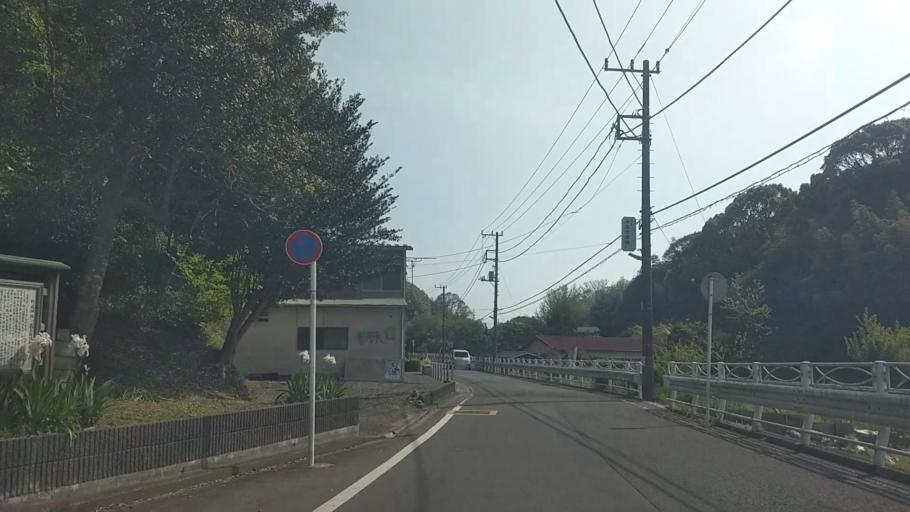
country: JP
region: Kanagawa
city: Kamakura
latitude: 35.3851
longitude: 139.5656
